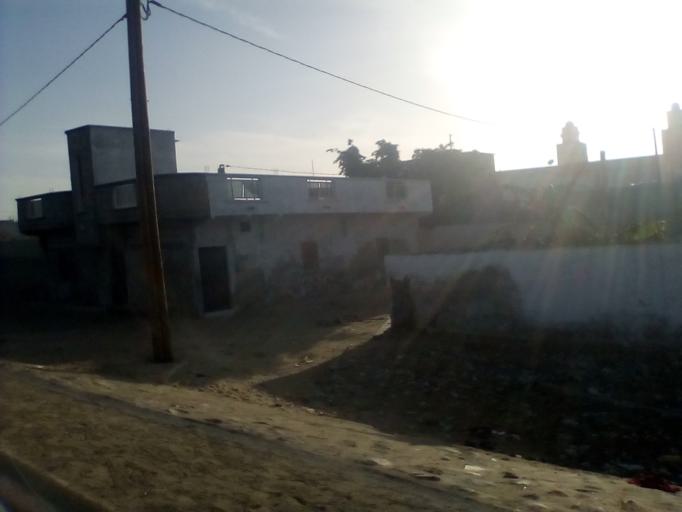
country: SN
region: Saint-Louis
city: Saint-Louis
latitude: 15.9957
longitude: -16.4832
